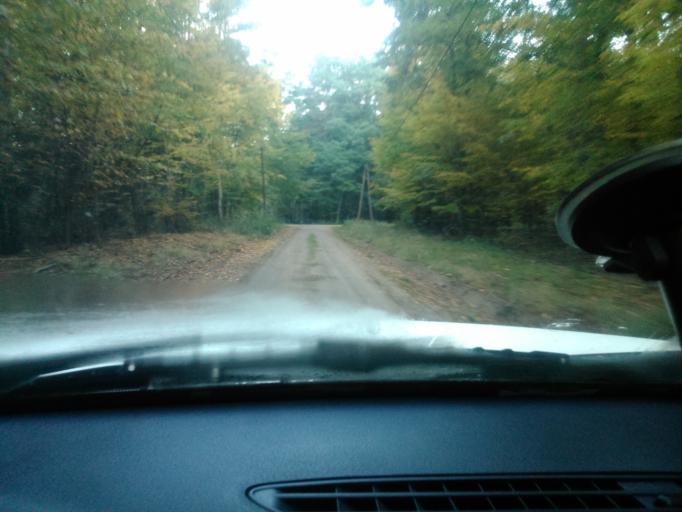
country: PL
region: Kujawsko-Pomorskie
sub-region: Powiat golubsko-dobrzynski
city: Golub-Dobrzyn
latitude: 53.1450
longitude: 19.1291
